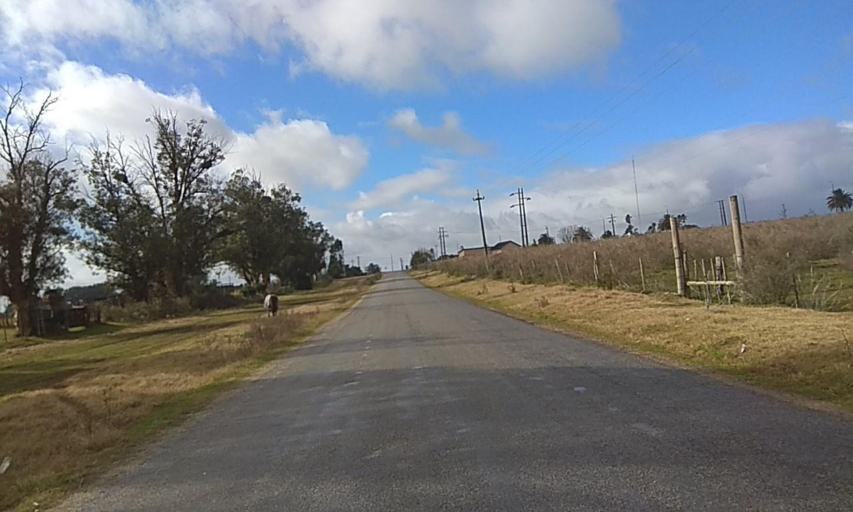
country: UY
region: Florida
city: Florida
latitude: -34.0947
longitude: -56.1925
